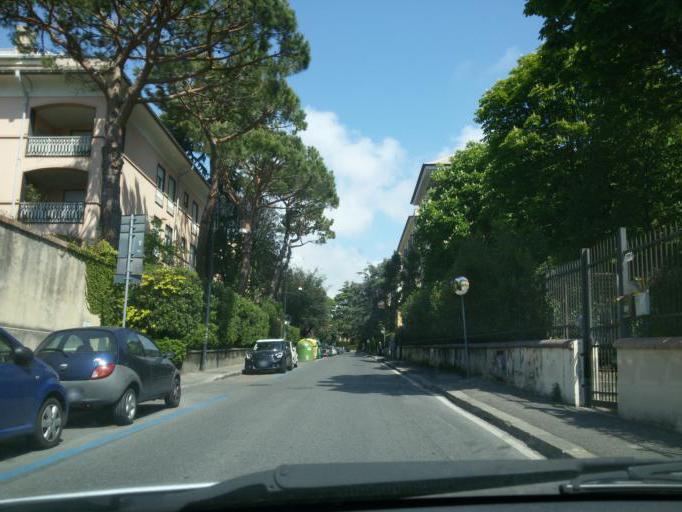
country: IT
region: Liguria
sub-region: Provincia di Genova
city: San Teodoro
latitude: 44.3971
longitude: 8.9588
